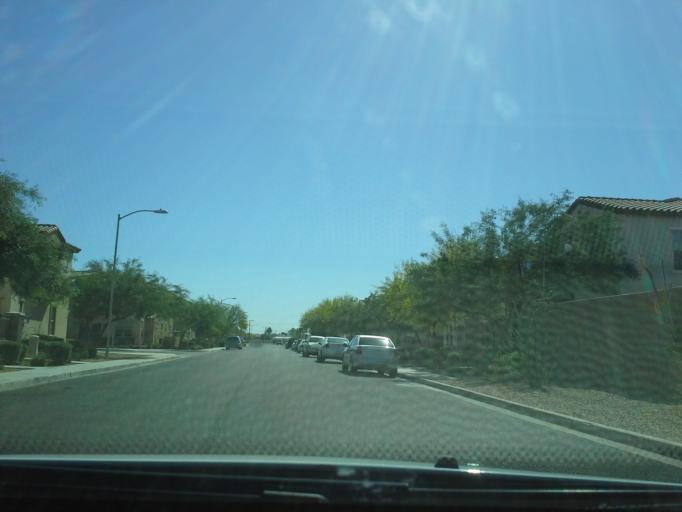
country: US
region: Arizona
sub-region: Maricopa County
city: Phoenix
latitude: 33.4376
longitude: -112.0949
